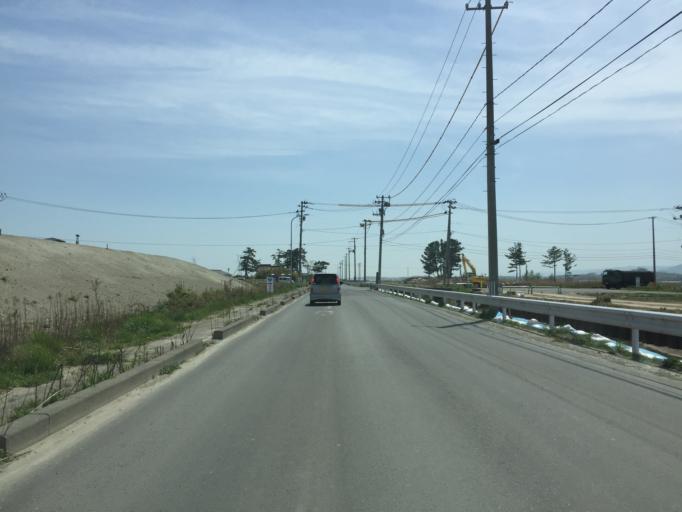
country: JP
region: Miyagi
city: Watari
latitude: 37.9597
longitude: 140.9092
